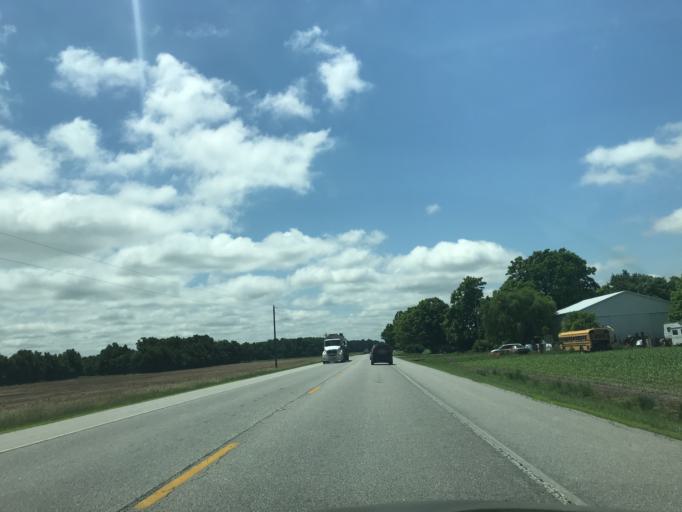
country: US
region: Maryland
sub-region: Caroline County
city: Federalsburg
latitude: 38.7775
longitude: -75.7875
